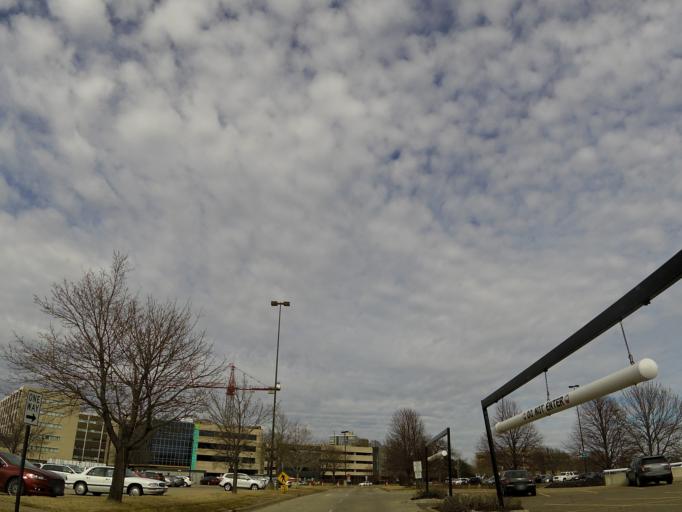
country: US
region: Minnesota
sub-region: Hennepin County
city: Edina
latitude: 44.8825
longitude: -93.3282
